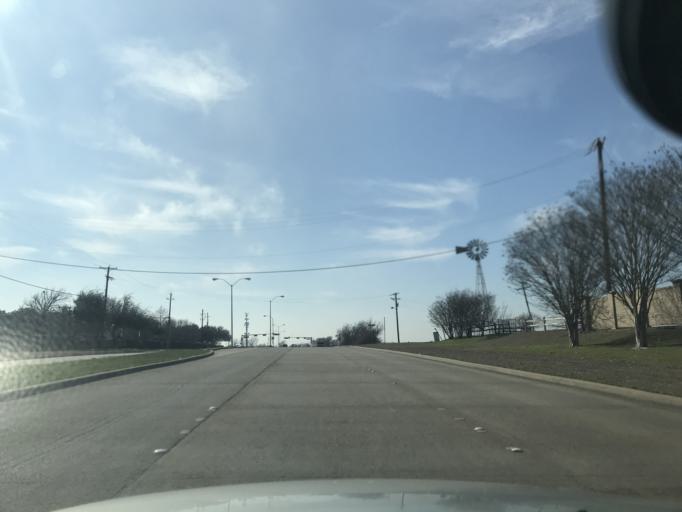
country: US
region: Texas
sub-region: Collin County
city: Parker
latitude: 33.0489
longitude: -96.6567
